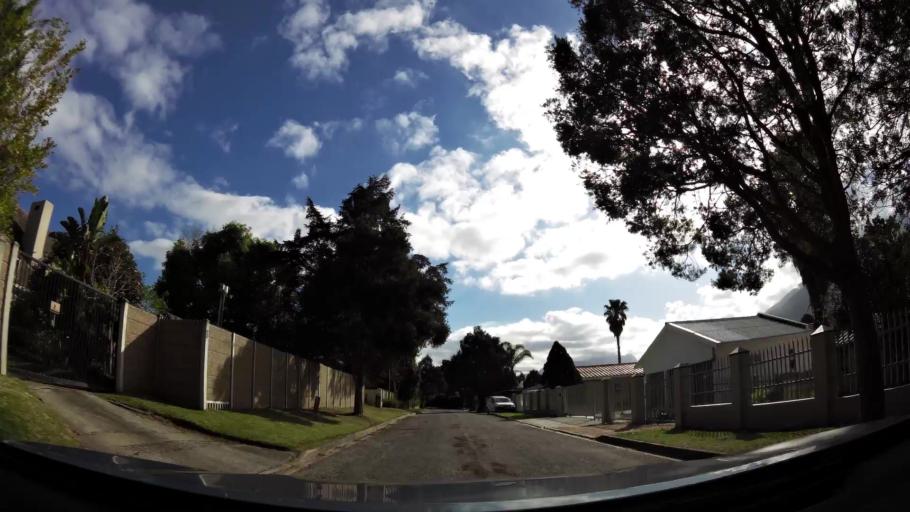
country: ZA
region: Western Cape
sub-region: Eden District Municipality
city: George
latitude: -33.9555
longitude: 22.4786
